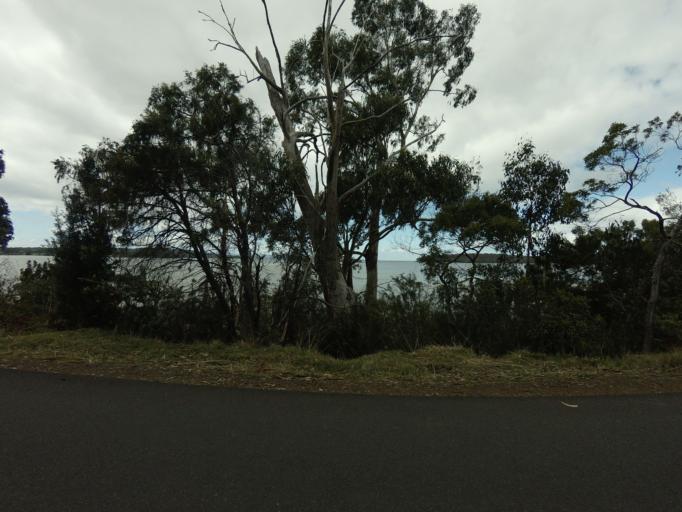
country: AU
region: Tasmania
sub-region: Huon Valley
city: Geeveston
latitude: -43.4451
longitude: 146.9615
